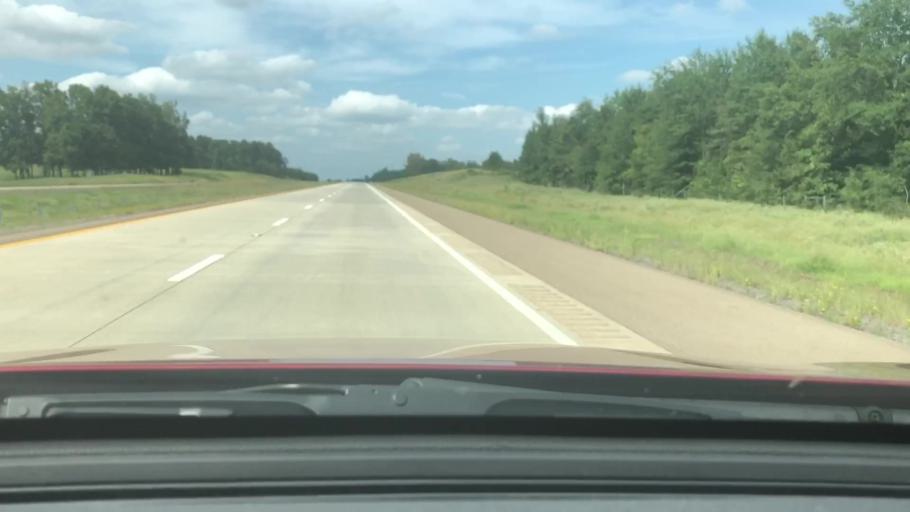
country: US
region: Louisiana
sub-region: Caddo Parish
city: Vivian
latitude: 33.0385
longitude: -93.8998
